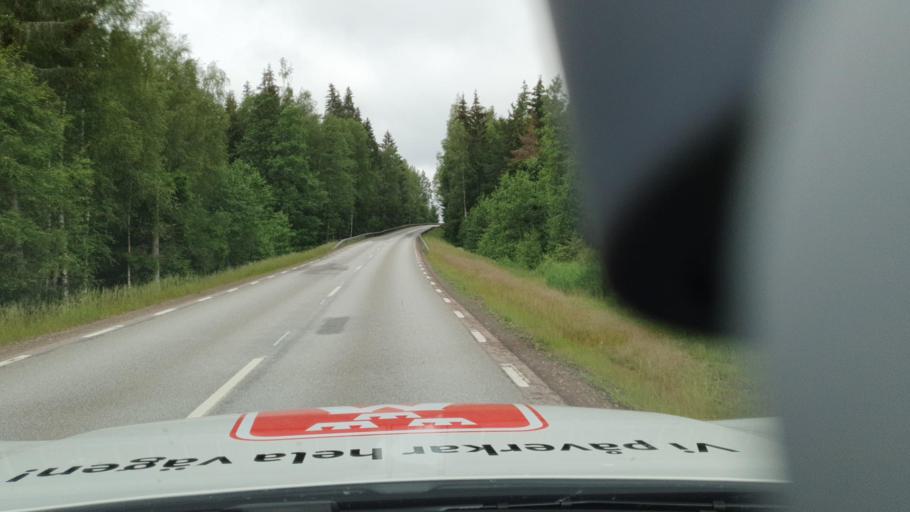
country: SE
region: Vaermland
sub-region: Kristinehamns Kommun
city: Bjorneborg
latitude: 59.1103
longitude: 14.2222
